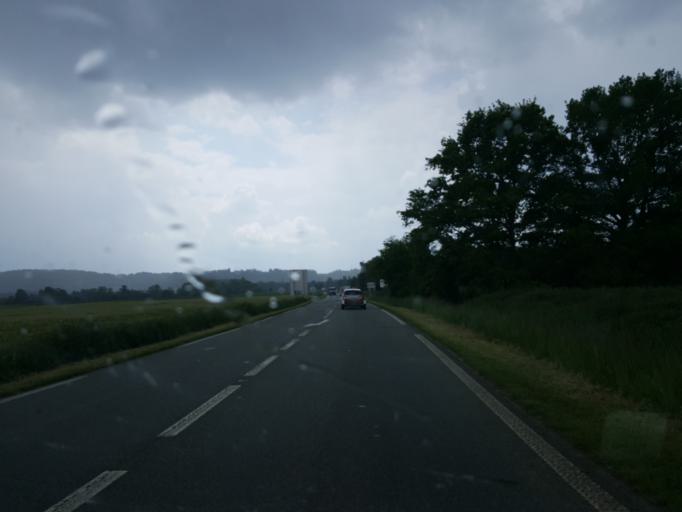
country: FR
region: Picardie
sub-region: Departement de l'Oise
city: Auneuil
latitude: 49.3884
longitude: 2.0058
